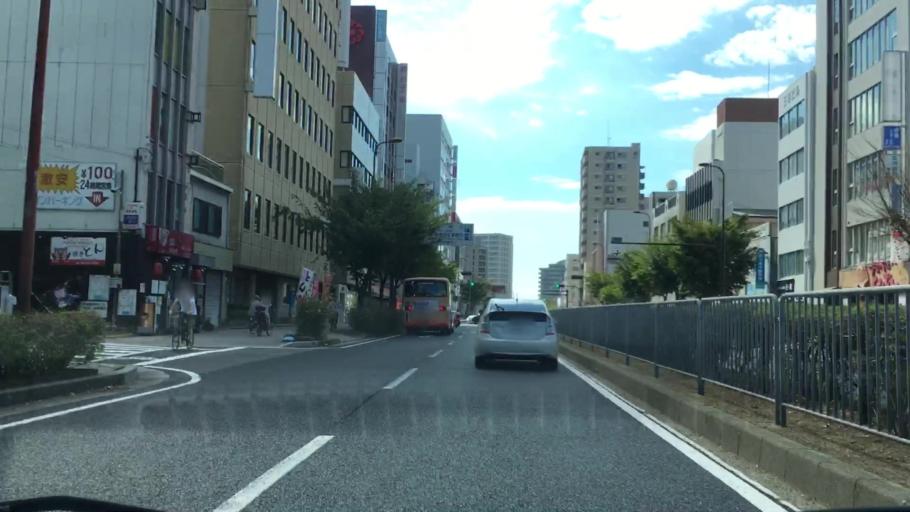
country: JP
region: Hyogo
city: Akashi
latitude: 34.6478
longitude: 134.9897
